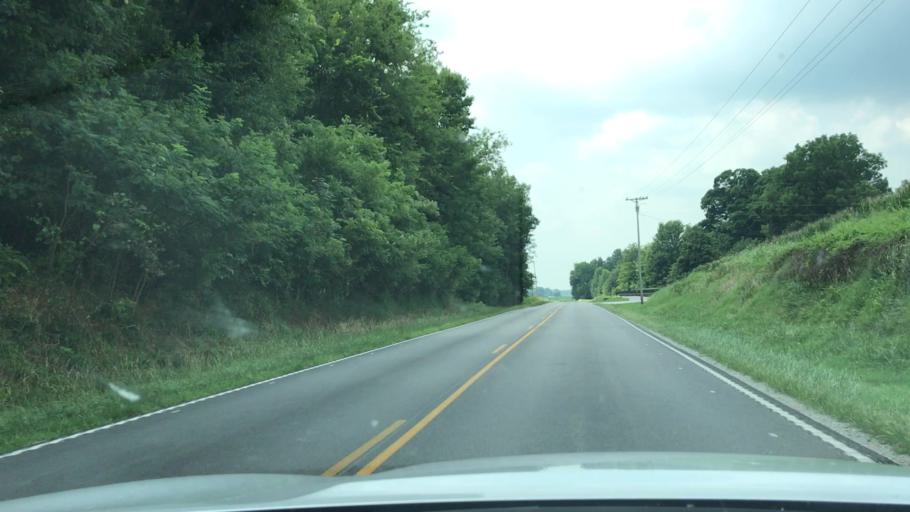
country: US
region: Kentucky
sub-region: Todd County
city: Guthrie
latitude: 36.7075
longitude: -87.1056
